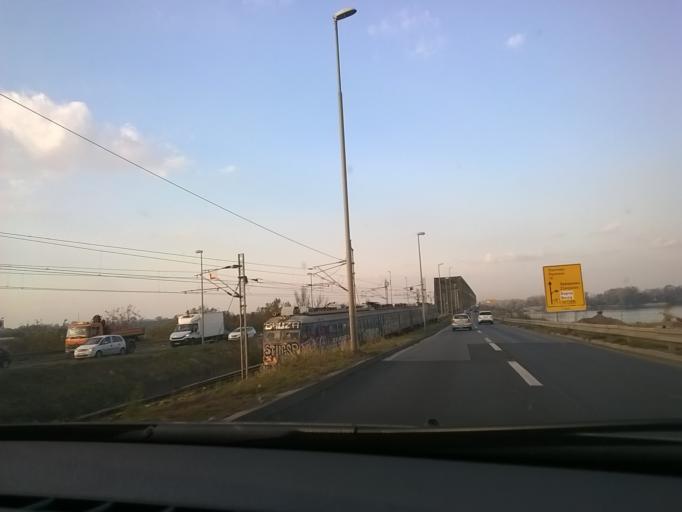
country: RS
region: Central Serbia
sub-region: Belgrade
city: Palilula
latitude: 44.8225
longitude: 20.4910
